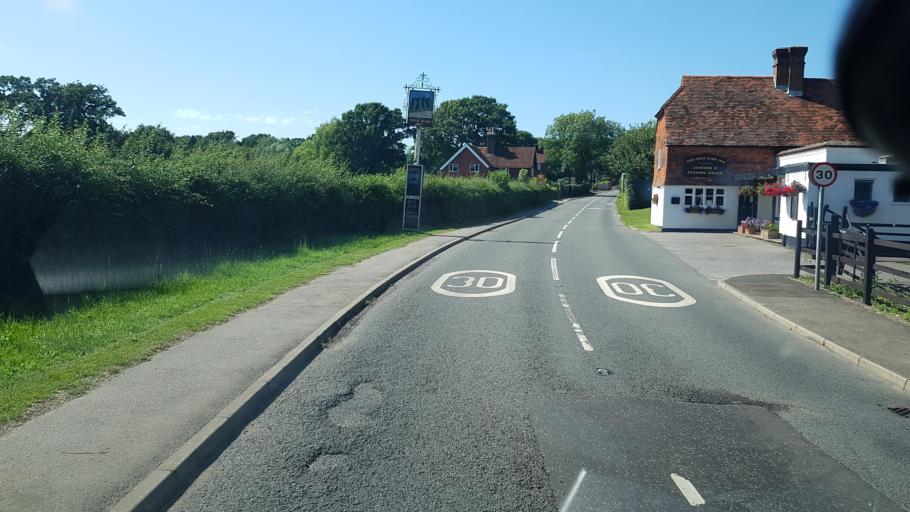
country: GB
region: England
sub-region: Kent
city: Edenbridge
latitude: 51.2147
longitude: 0.1016
